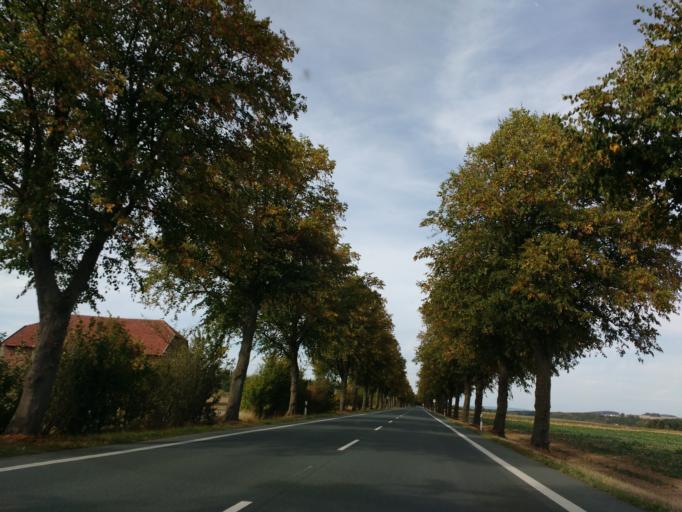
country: DE
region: North Rhine-Westphalia
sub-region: Regierungsbezirk Detmold
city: Willebadessen
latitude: 51.6080
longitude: 9.1338
